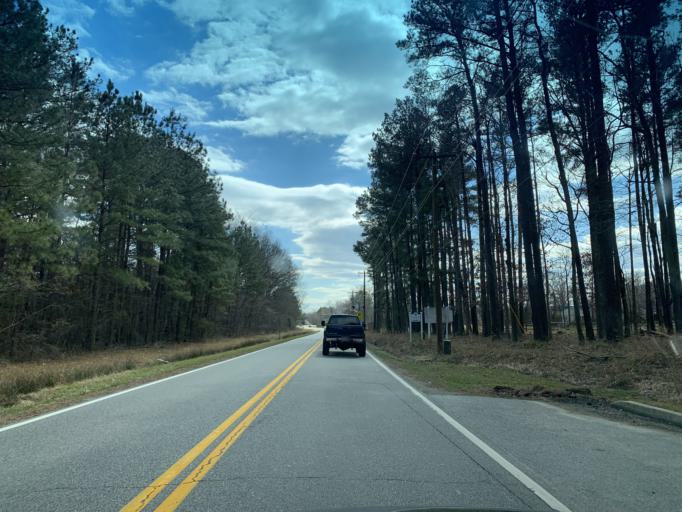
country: US
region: Maryland
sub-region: Queen Anne's County
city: Stevensville
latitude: 38.9932
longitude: -76.3119
